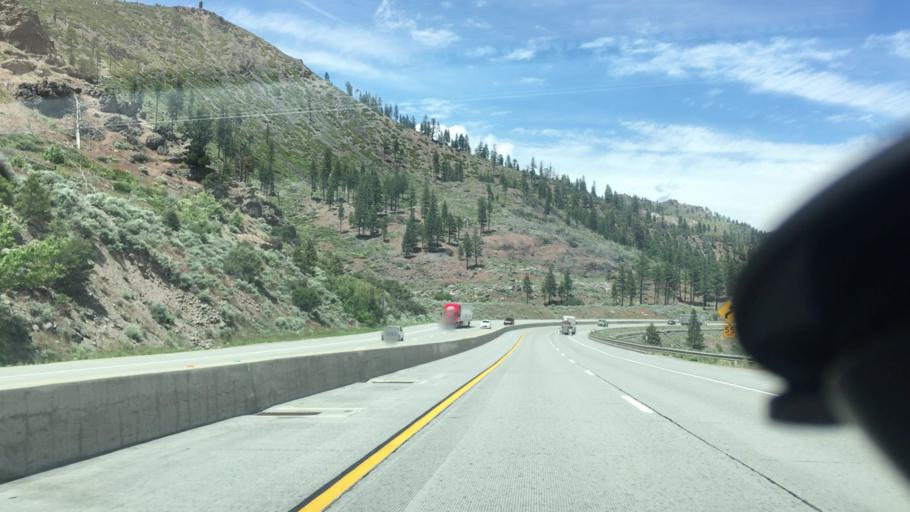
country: US
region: Nevada
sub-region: Washoe County
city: Verdi
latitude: 39.3838
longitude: -120.0236
